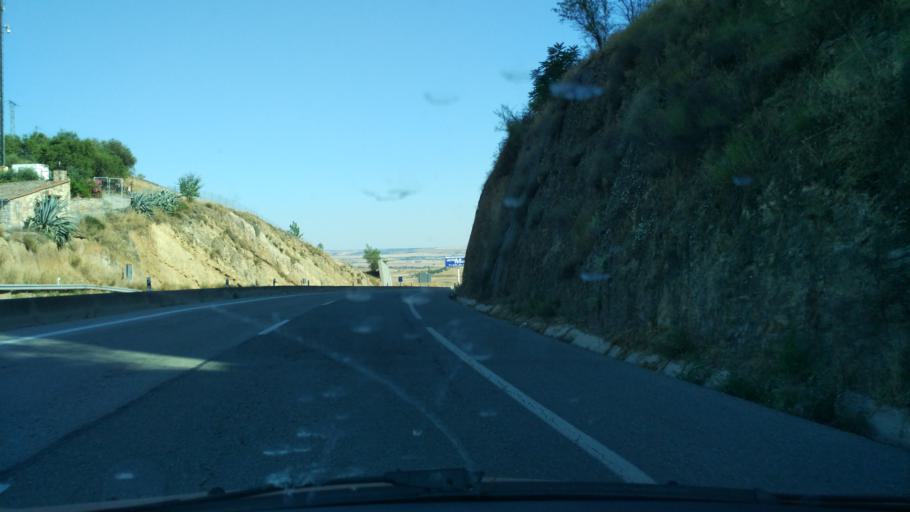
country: ES
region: Madrid
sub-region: Provincia de Madrid
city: El Molar
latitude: 40.7295
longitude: -3.5808
